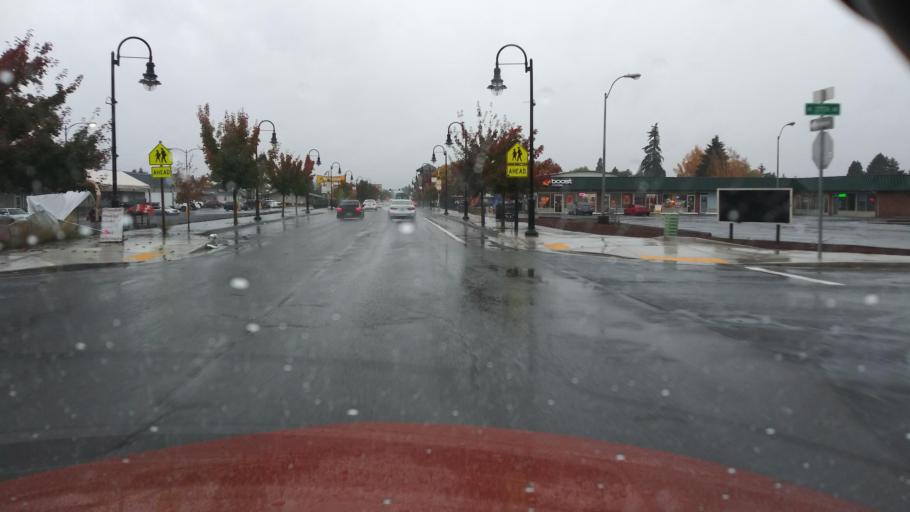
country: US
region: Oregon
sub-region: Washington County
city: Cornelius
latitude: 45.5209
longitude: -123.0512
